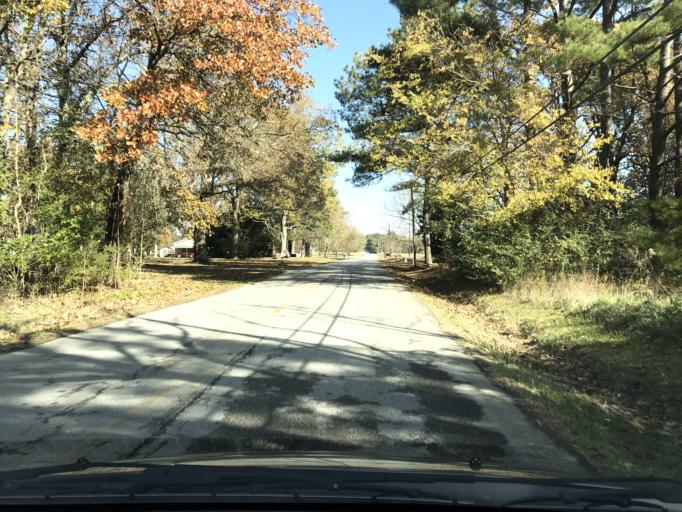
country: US
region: Tennessee
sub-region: Coffee County
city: Tullahoma
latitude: 35.3982
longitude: -86.1628
